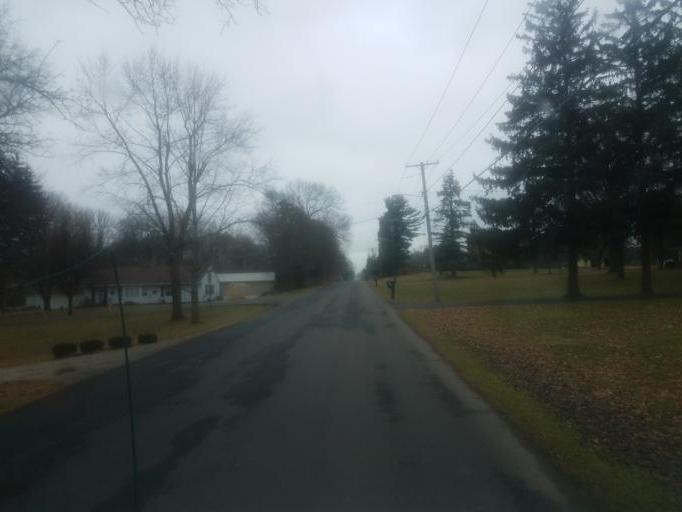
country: US
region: Ohio
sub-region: Crawford County
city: Galion
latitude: 40.7460
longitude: -82.7832
